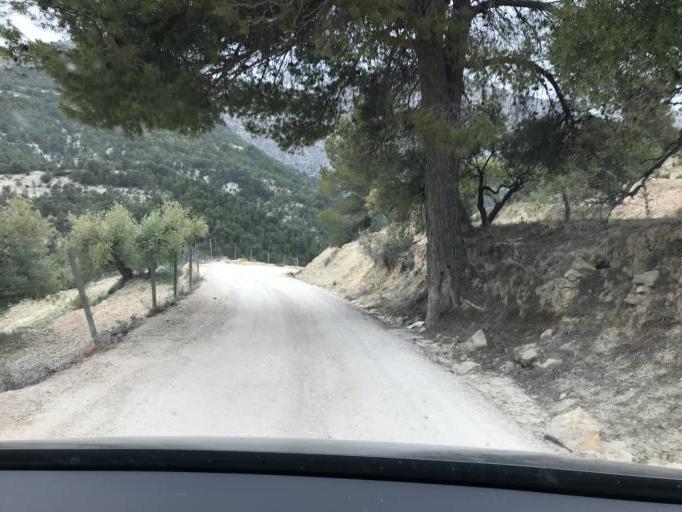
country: ES
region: Andalusia
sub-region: Provincia de Granada
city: Castril
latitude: 37.8307
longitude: -2.7731
